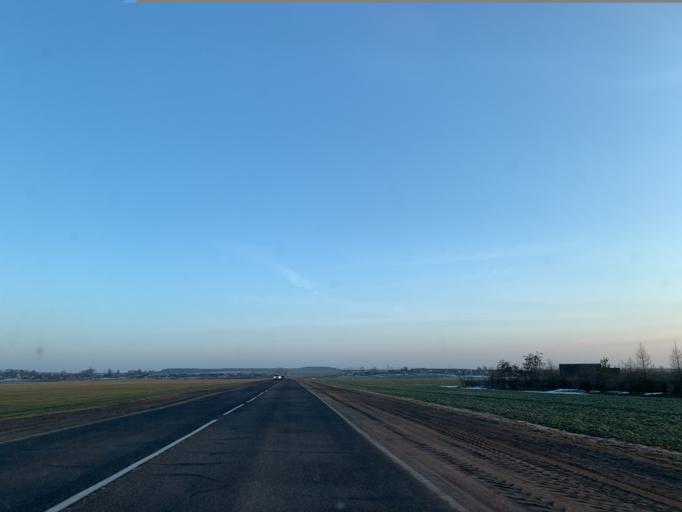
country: BY
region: Minsk
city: Haradzyeya
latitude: 53.3109
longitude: 26.5669
